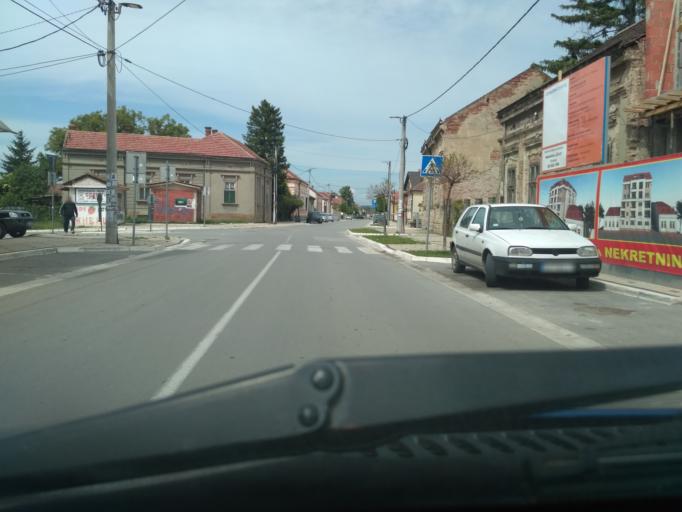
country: RS
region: Central Serbia
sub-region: Pomoravski Okrug
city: Svilajnac
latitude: 44.2366
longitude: 21.1969
